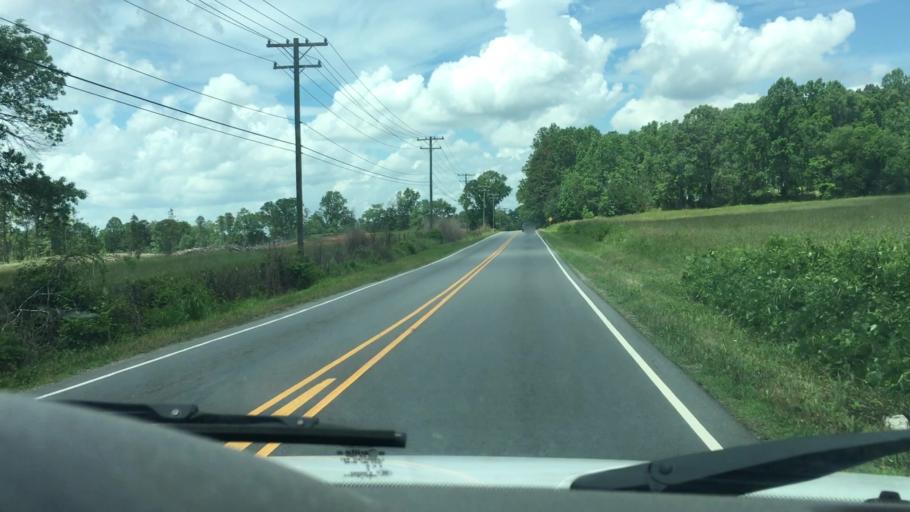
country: US
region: North Carolina
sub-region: Mecklenburg County
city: Huntersville
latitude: 35.4191
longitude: -80.7476
